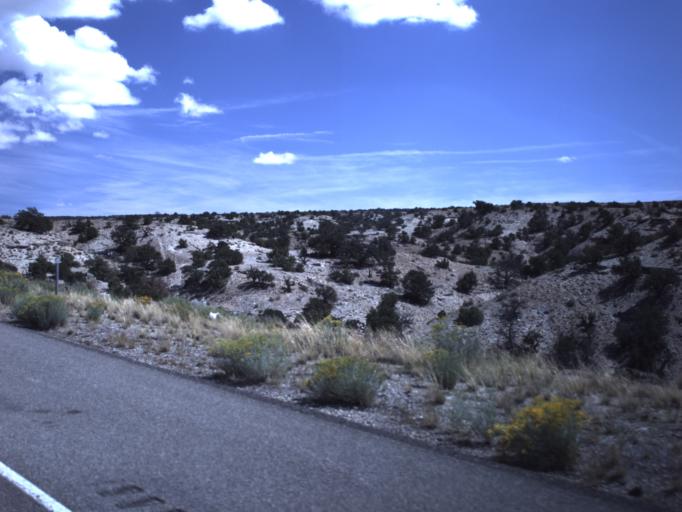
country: US
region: Utah
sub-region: Emery County
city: Ferron
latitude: 38.8436
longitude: -110.9783
